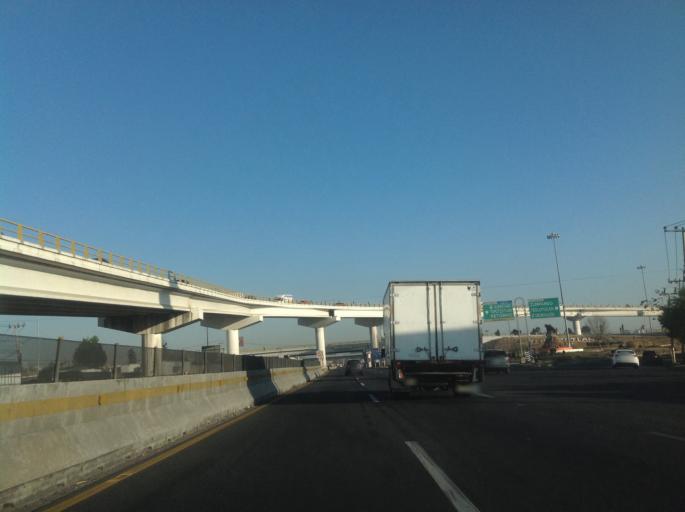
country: MX
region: Mexico
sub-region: Cuautitlan
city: San Jose del Puente
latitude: 19.7100
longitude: -99.2065
